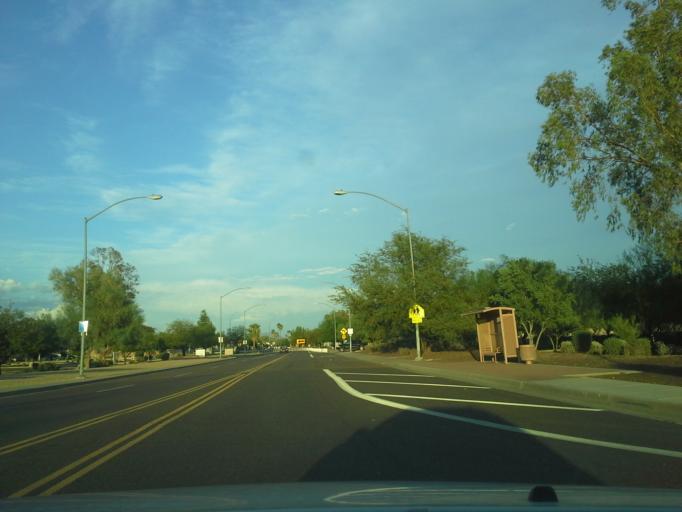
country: US
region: Arizona
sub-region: Maricopa County
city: Glendale
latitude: 33.6619
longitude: -112.1110
